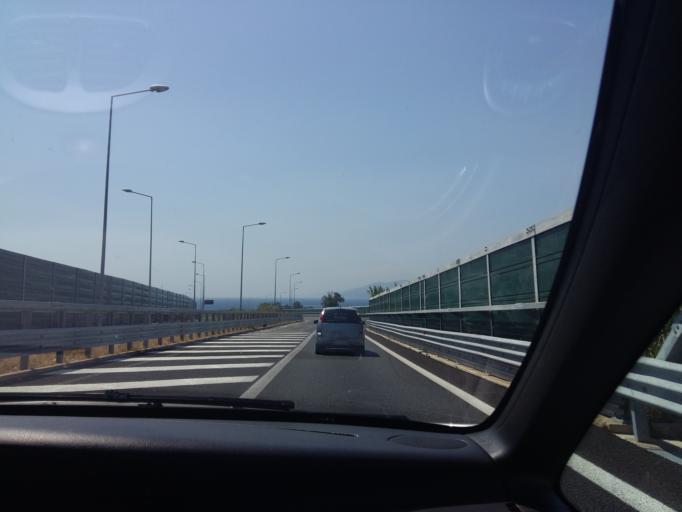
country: IT
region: Calabria
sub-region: Provincia di Reggio Calabria
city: Campo Calabro
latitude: 38.2098
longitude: 15.6427
